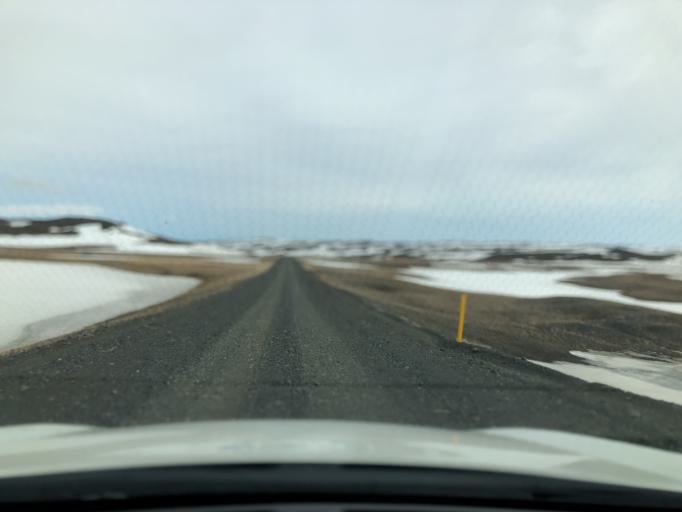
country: IS
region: East
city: Egilsstadir
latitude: 65.2953
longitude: -15.4399
